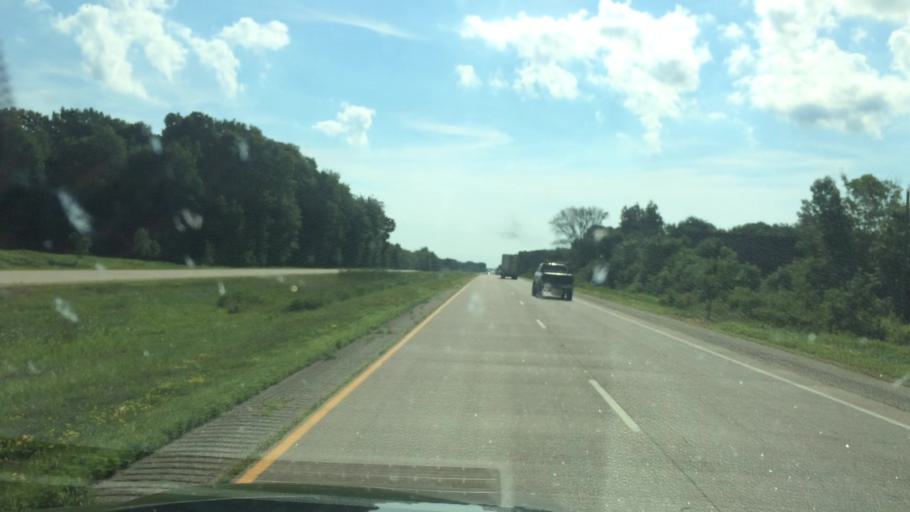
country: US
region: Wisconsin
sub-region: Waupaca County
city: Marion
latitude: 44.8040
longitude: -88.9807
